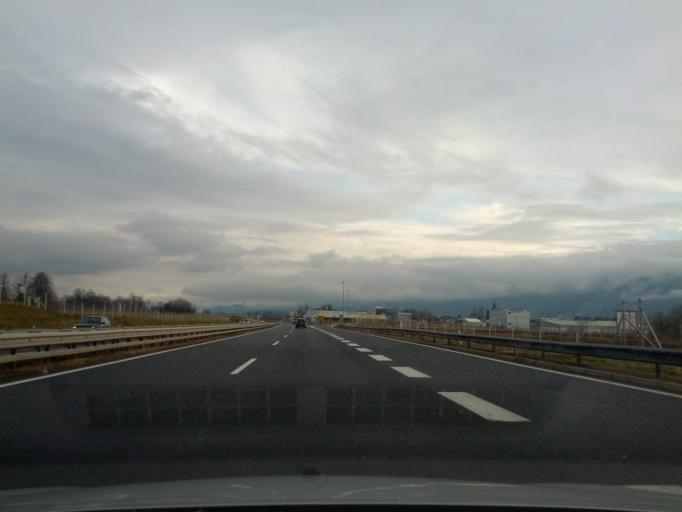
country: SI
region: Radovljica
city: Lesce
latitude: 46.3709
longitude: 14.1582
